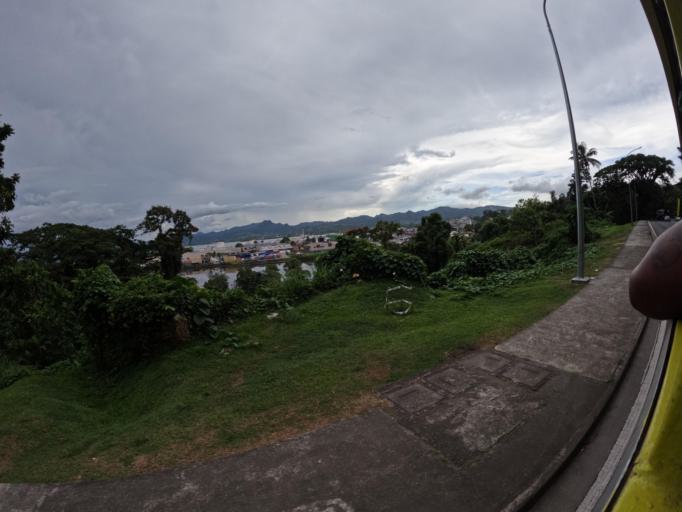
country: FJ
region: Central
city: Suva
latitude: -18.1324
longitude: 178.4331
